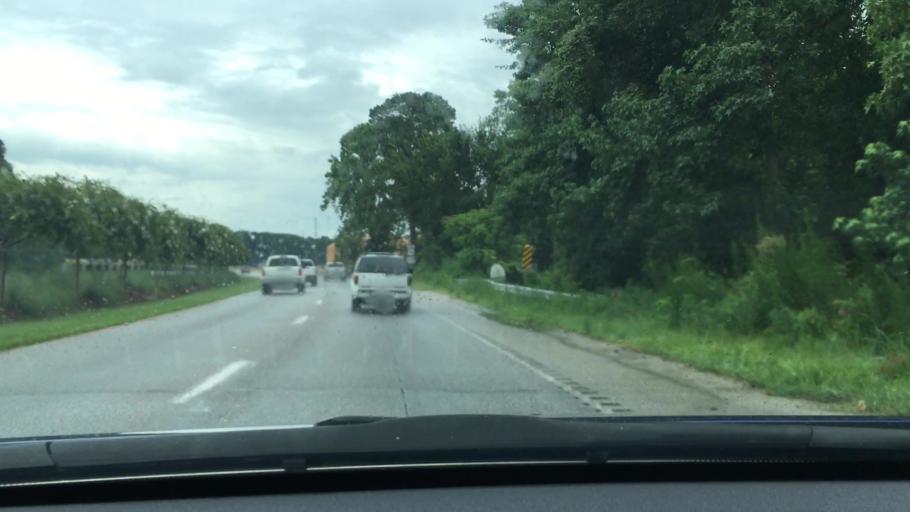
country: US
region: South Carolina
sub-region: Sumter County
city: Cherryvale
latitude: 33.9615
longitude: -80.4270
